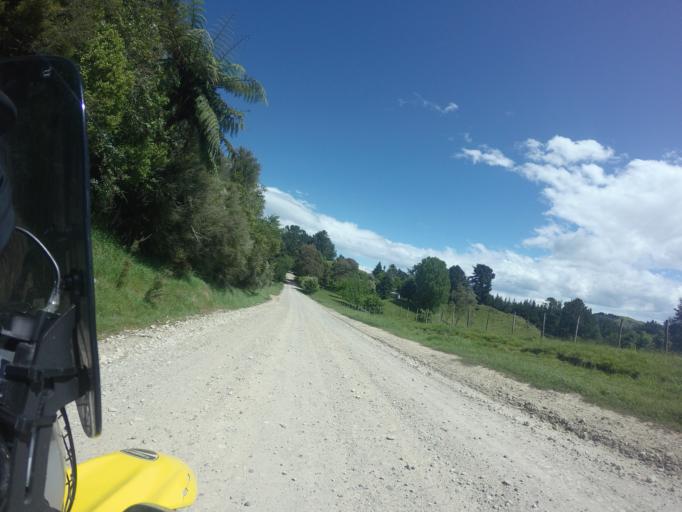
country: NZ
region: Hawke's Bay
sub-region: Wairoa District
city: Wairoa
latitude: -38.9749
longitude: 177.7036
